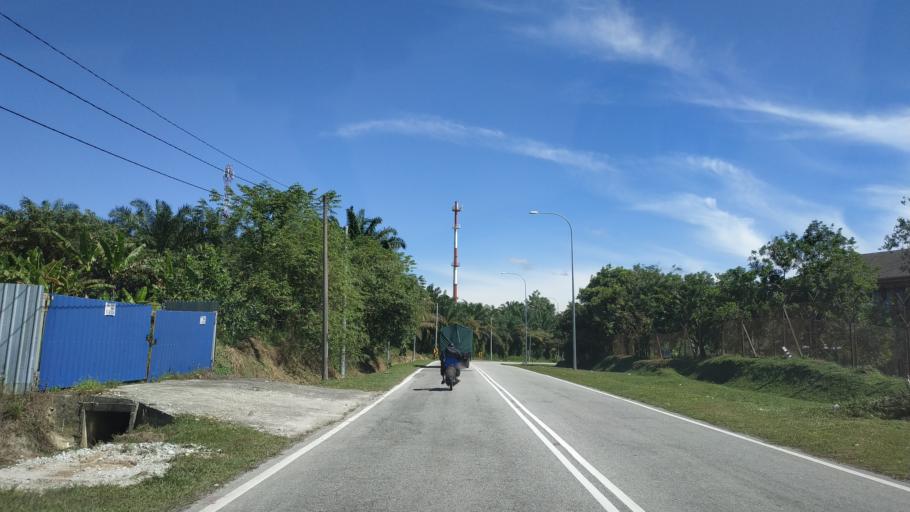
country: MY
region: Kedah
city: Kulim
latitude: 5.3328
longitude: 100.5349
